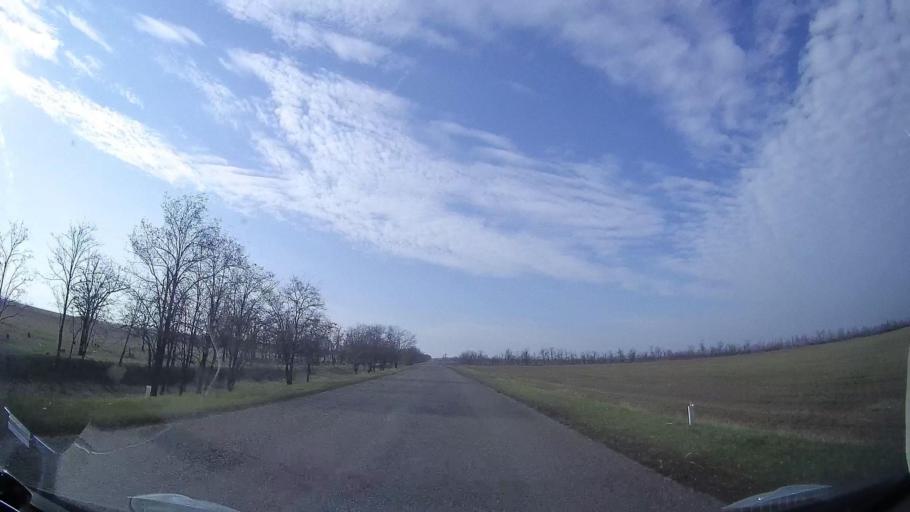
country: RU
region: Rostov
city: Gigant
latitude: 46.8509
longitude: 41.3164
